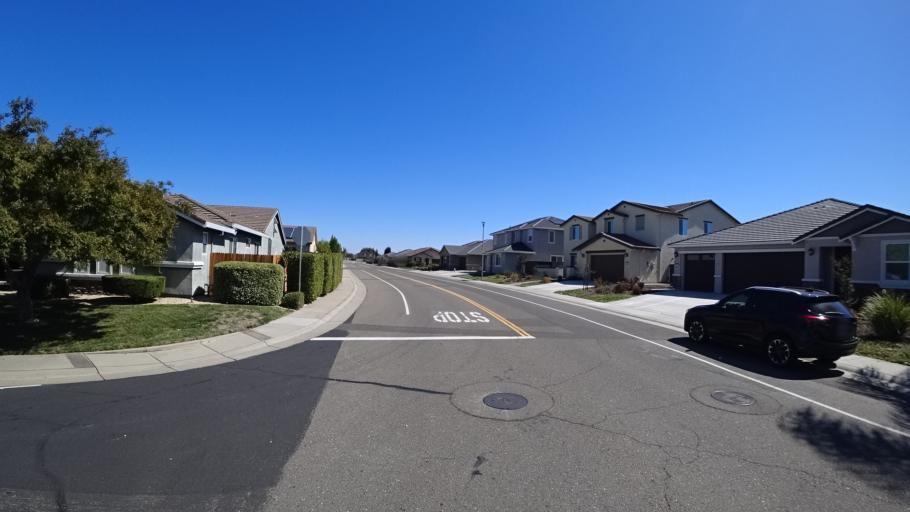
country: US
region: California
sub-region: Sacramento County
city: Elk Grove
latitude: 38.4183
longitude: -121.3393
